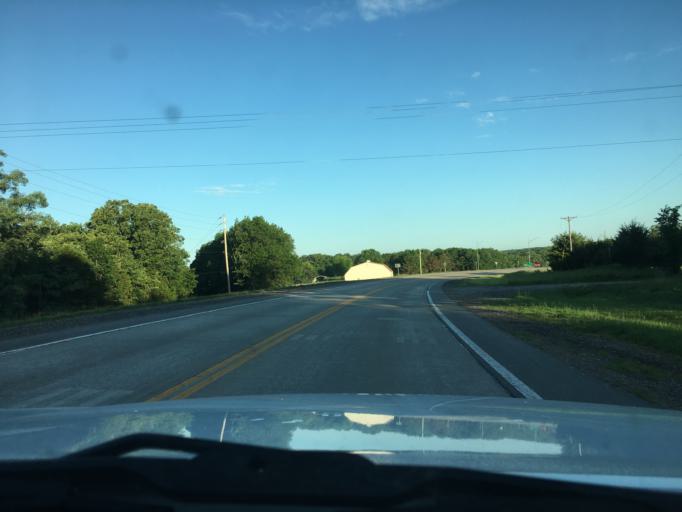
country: US
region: Missouri
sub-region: Franklin County
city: Gerald
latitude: 38.3876
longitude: -91.4136
